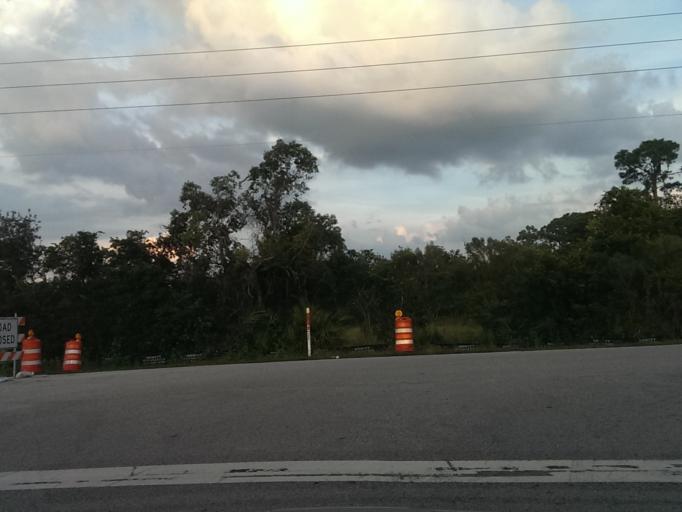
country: US
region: Florida
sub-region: Orange County
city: Lake Butler
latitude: 28.4676
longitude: -81.5829
